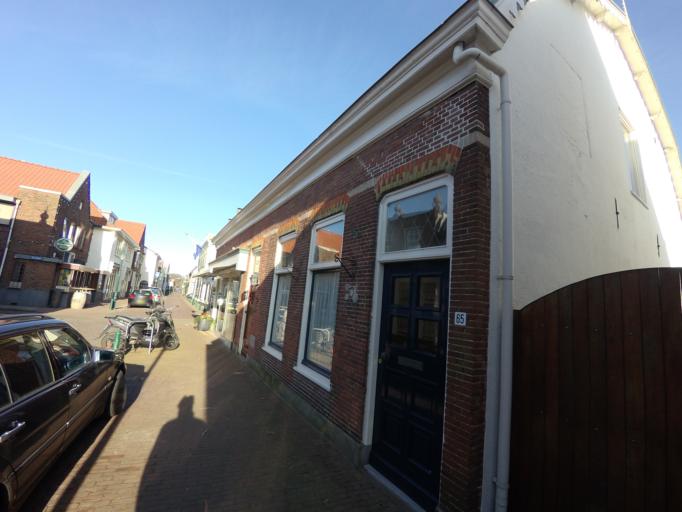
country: NL
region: South Holland
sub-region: Gemeente Teylingen
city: Voorhout
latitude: 52.1977
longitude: 4.5054
